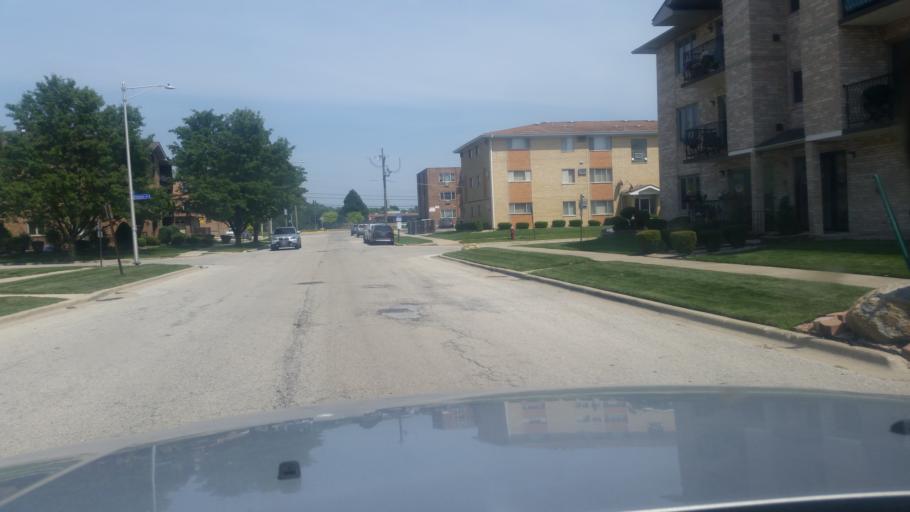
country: US
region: Illinois
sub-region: Cook County
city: Oak Lawn
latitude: 41.6997
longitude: -87.7613
